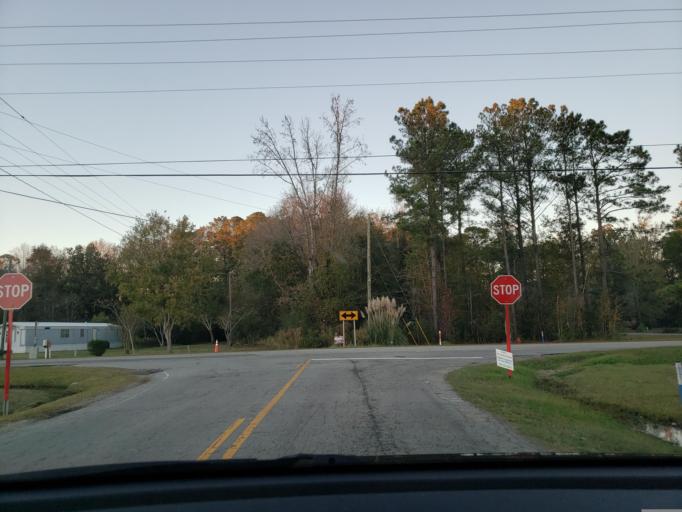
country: US
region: North Carolina
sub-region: Onslow County
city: Jacksonville
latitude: 34.7336
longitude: -77.5835
